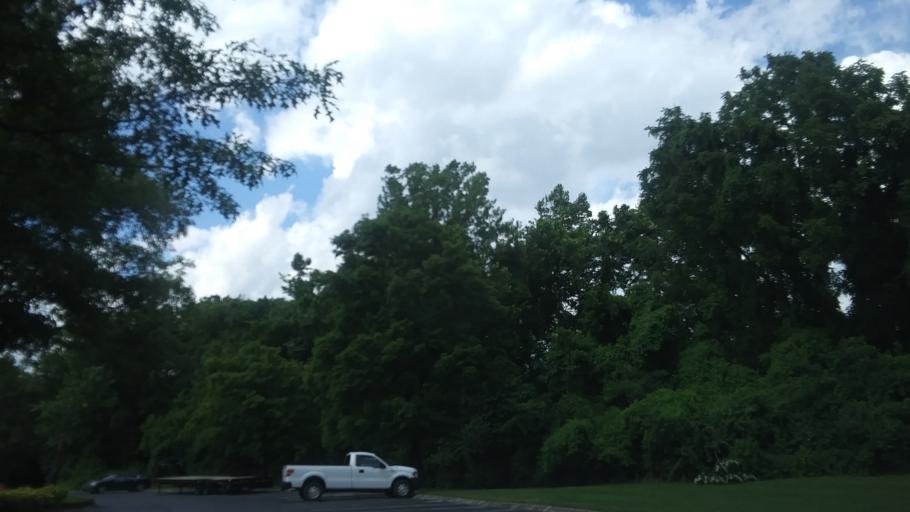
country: US
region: Tennessee
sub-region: Davidson County
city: Oak Hill
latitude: 36.0881
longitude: -86.6992
